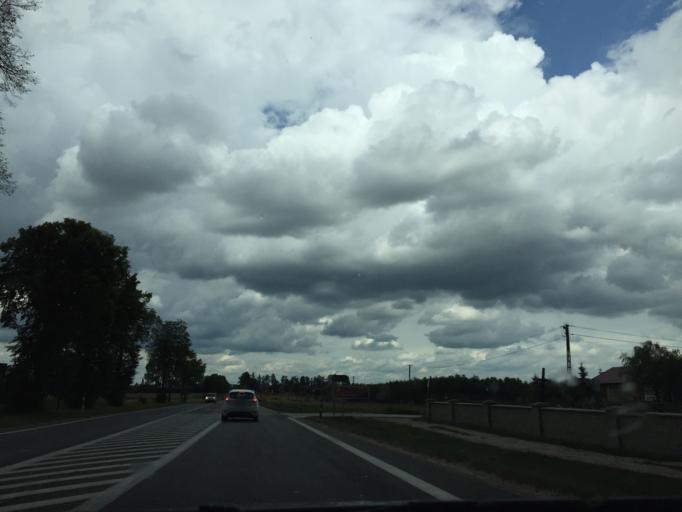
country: PL
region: Swietokrzyskie
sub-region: Powiat jedrzejowski
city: Jedrzejow
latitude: 50.6912
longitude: 20.3617
